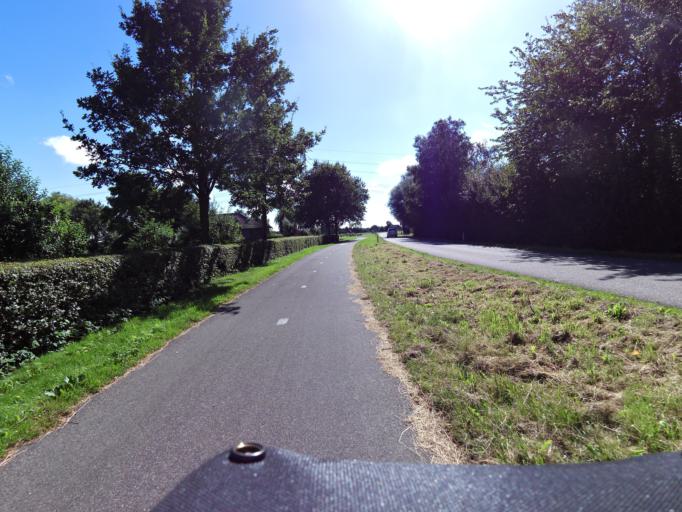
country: NL
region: South Holland
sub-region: Gemeente Spijkenisse
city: Spijkenisse
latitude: 51.8347
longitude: 4.2848
